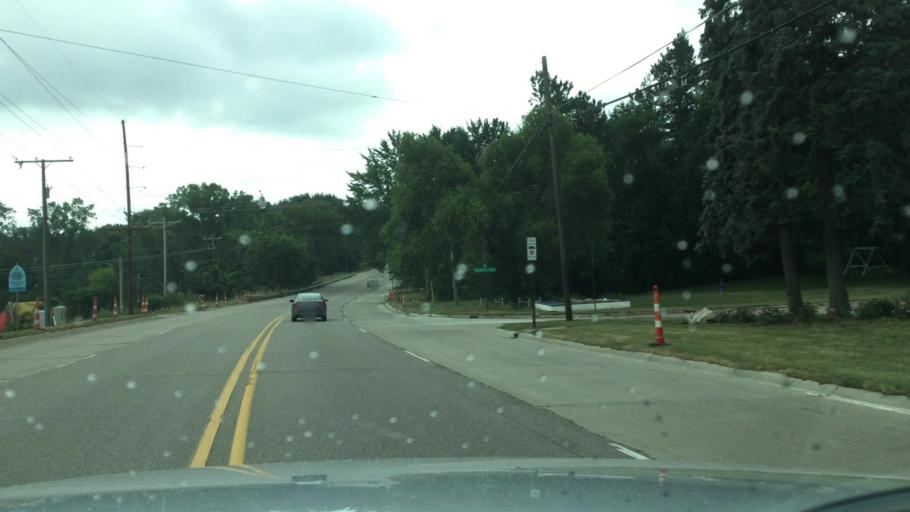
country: US
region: Michigan
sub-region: Genesee County
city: Flint
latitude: 43.0284
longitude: -83.7608
